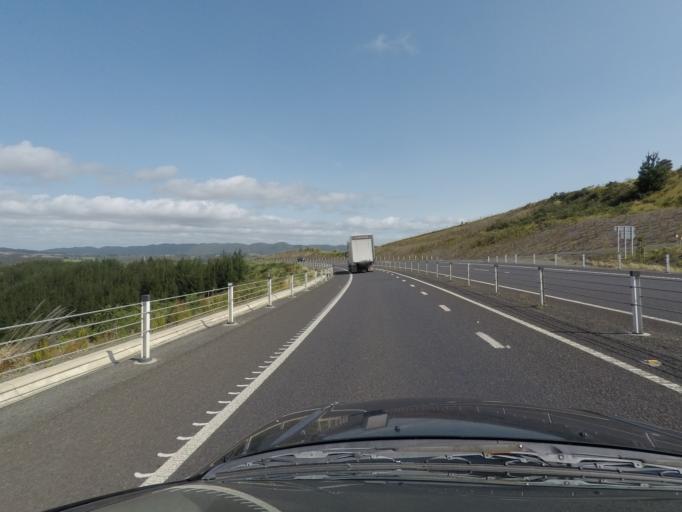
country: NZ
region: Northland
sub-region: Whangarei
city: Ruakaka
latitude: -36.0545
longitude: 174.4250
